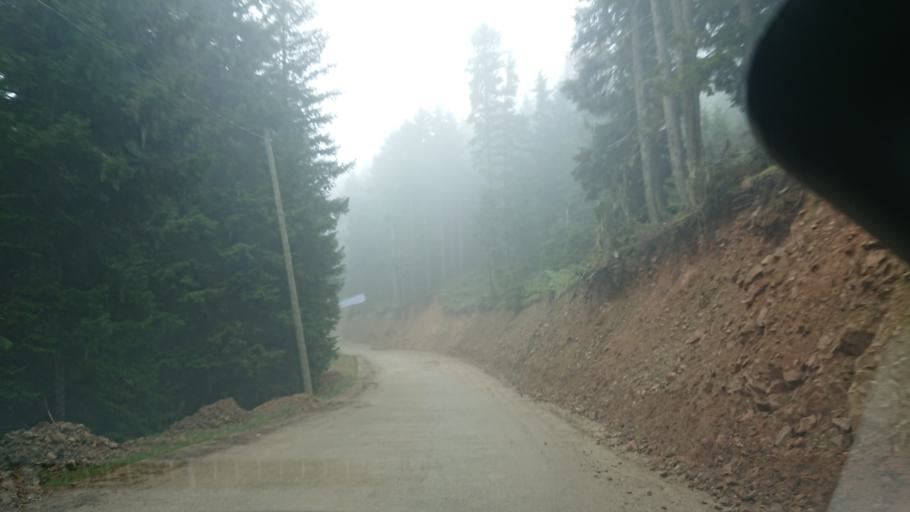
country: TR
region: Gumushane
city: Kurtun
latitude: 40.6709
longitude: 39.0002
